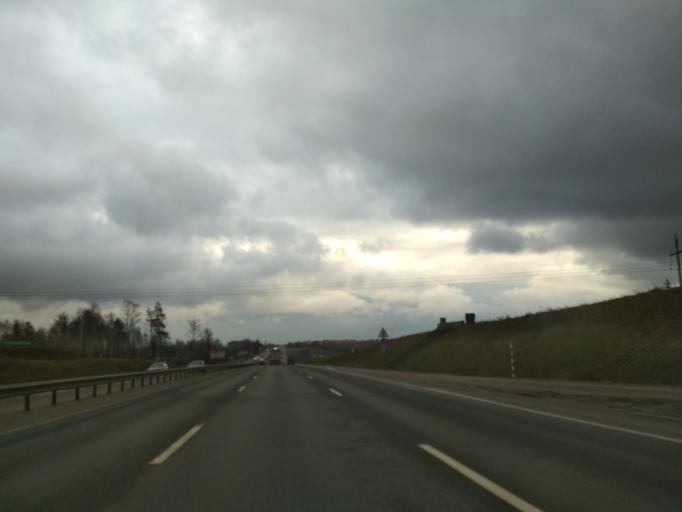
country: BY
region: Minsk
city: Pryvol'ny
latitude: 53.8131
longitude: 27.7762
